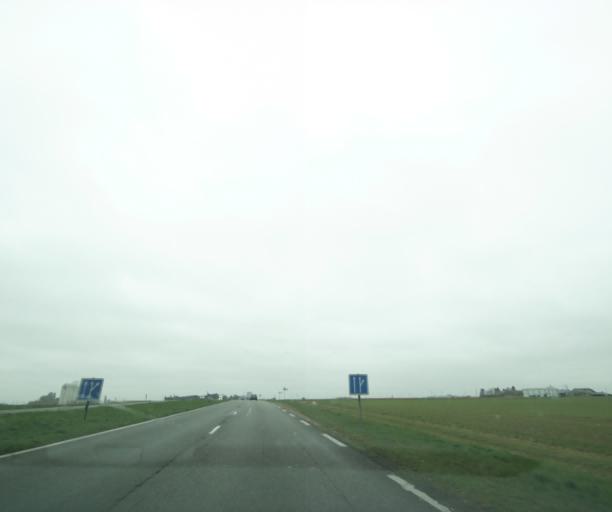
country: FR
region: Ile-de-France
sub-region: Departement de l'Essonne
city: Angerville
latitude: 48.2671
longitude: 1.9719
